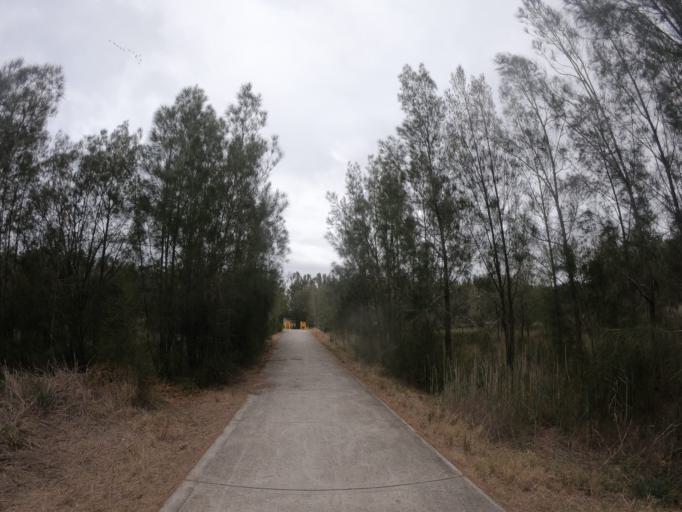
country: AU
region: New South Wales
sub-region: Wollongong
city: Berkeley
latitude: -34.4825
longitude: 150.8387
